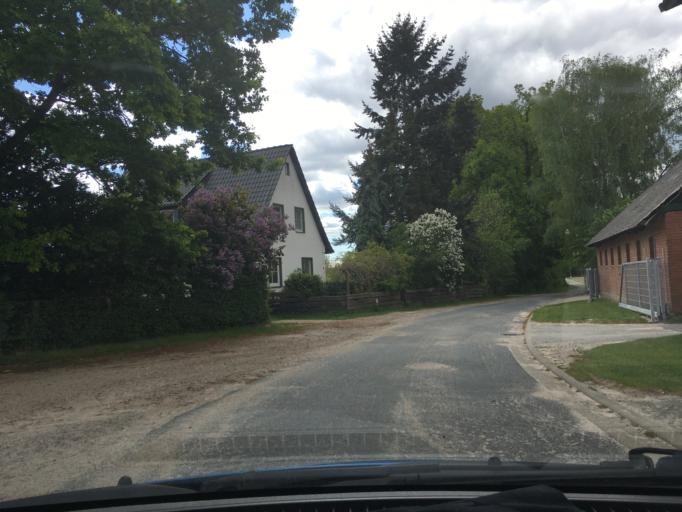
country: DE
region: Lower Saxony
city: Suderburg
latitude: 52.9352
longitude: 10.4876
